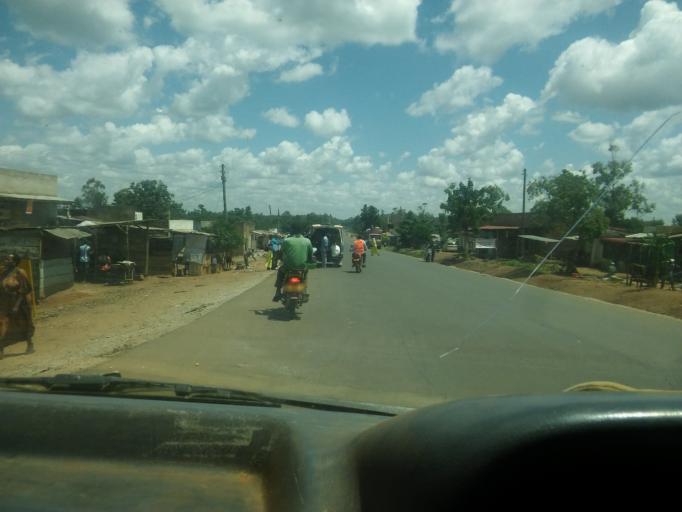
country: UG
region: Eastern Region
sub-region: Mbale District
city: Mbale
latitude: 1.0781
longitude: 34.1462
